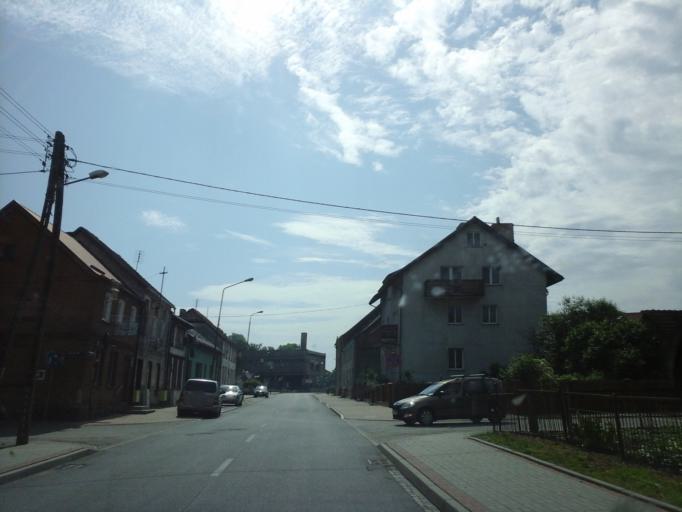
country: PL
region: West Pomeranian Voivodeship
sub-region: Powiat choszczenski
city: Drawno
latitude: 53.2209
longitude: 15.7572
